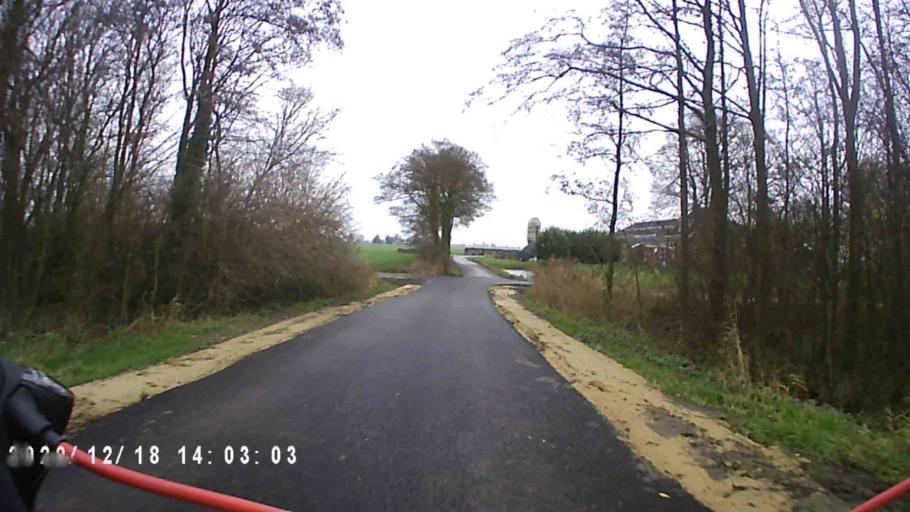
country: NL
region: Groningen
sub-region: Gemeente Bedum
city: Bedum
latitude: 53.2940
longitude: 6.6484
